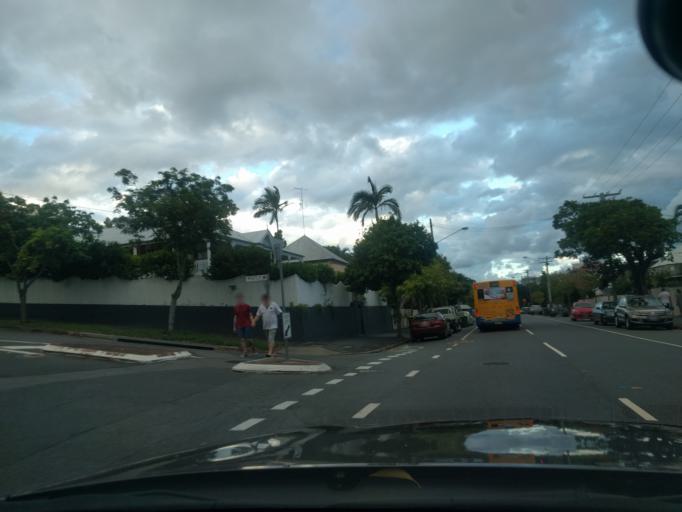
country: AU
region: Queensland
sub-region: Brisbane
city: Balmoral
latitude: -27.4652
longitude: 153.0481
